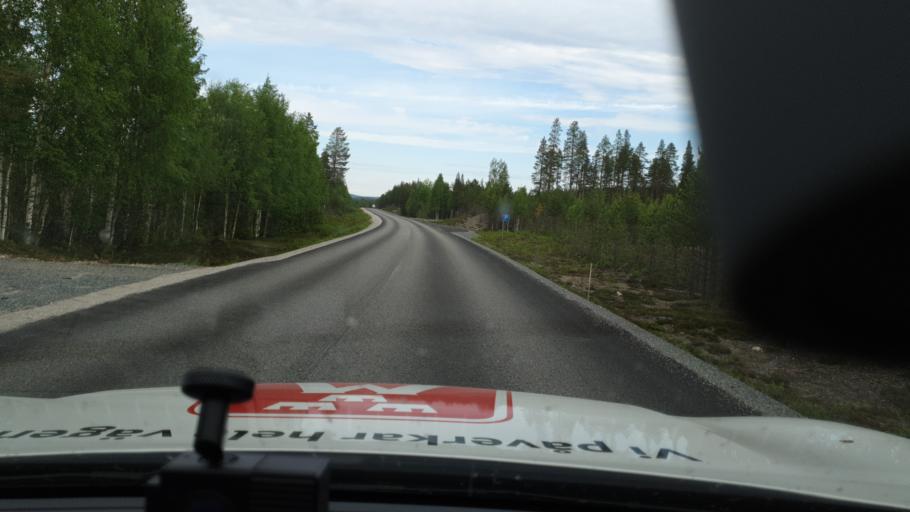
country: SE
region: Vaesterbotten
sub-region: Mala Kommun
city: Mala
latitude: 64.9686
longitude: 18.5795
